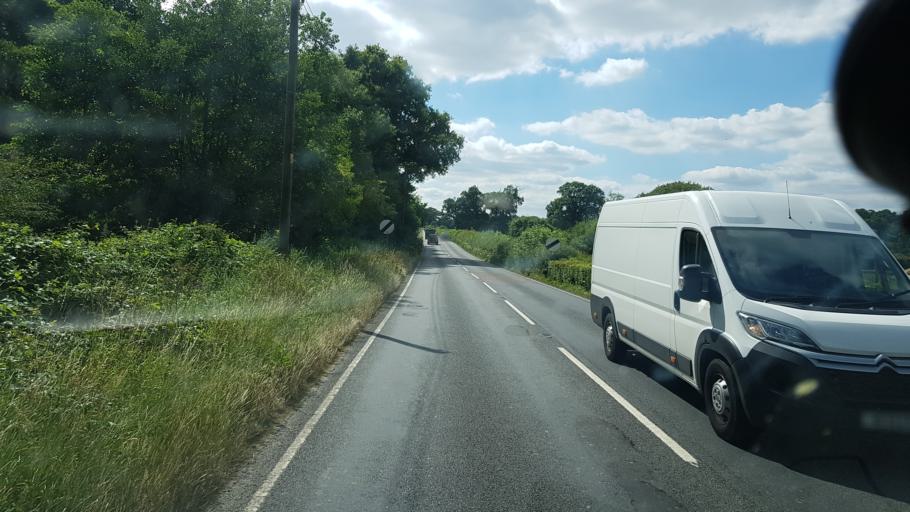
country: GB
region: England
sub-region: West Sussex
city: Southwater
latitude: 50.9930
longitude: -0.3464
